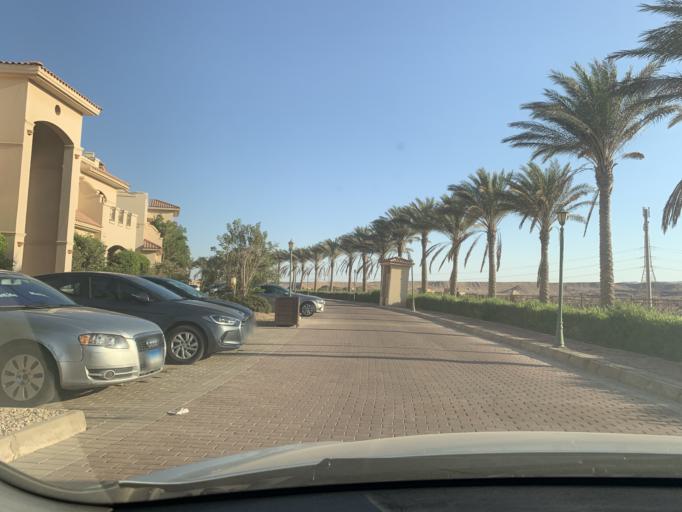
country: EG
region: As Suways
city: Ain Sukhna
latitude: 29.3732
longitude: 32.5685
